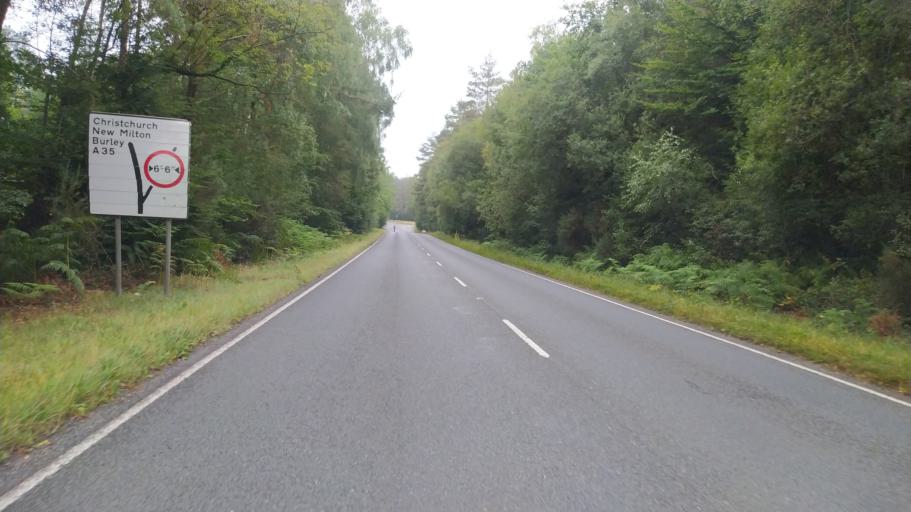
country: GB
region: England
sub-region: Hampshire
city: Lyndhurst
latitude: 50.8530
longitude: -1.6260
